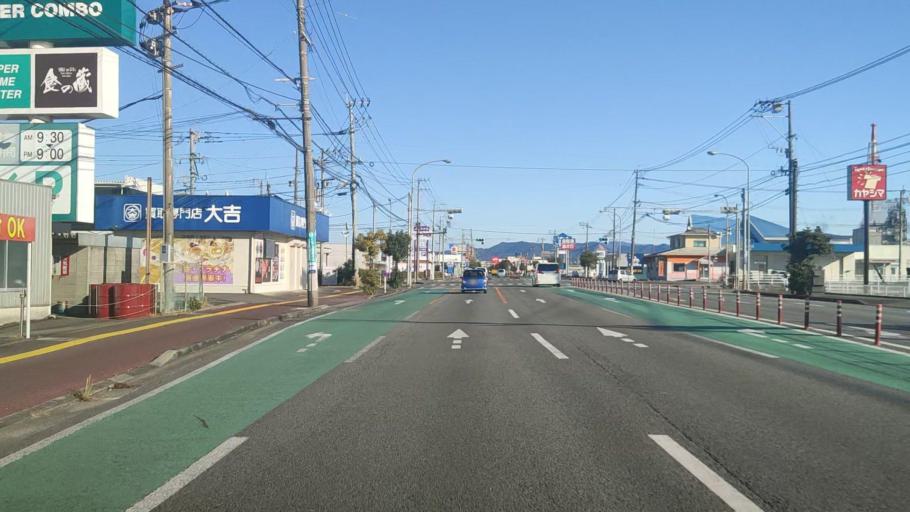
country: JP
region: Miyazaki
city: Nobeoka
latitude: 32.5619
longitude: 131.6812
